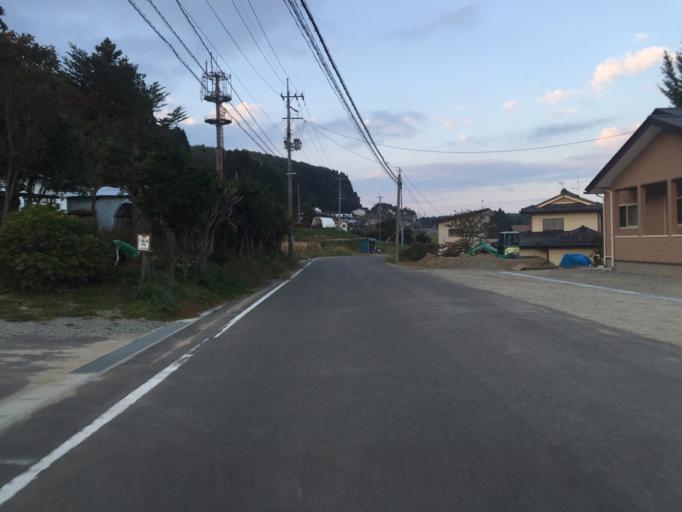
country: JP
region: Fukushima
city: Nihommatsu
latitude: 37.6102
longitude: 140.3565
